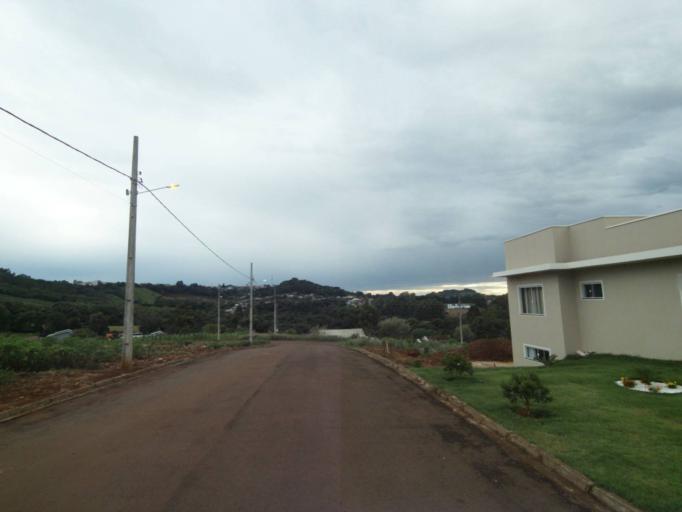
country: BR
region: Parana
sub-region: Guaraniacu
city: Guaraniacu
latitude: -25.1002
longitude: -52.8862
